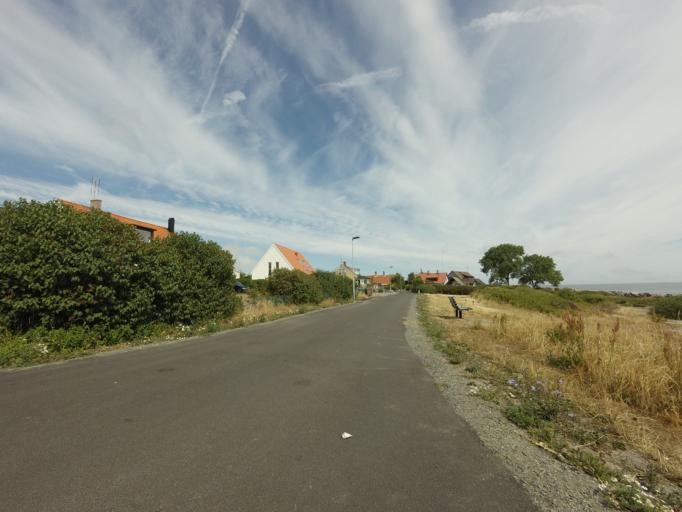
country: SE
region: Skane
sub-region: Simrishamns Kommun
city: Simrishamn
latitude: 55.5422
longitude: 14.3565
